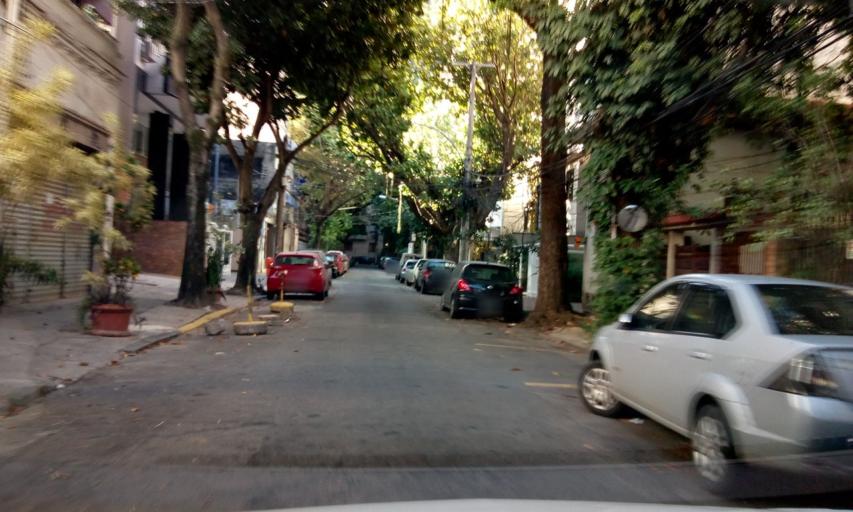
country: BR
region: Rio de Janeiro
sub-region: Rio De Janeiro
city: Rio de Janeiro
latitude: -22.9557
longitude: -43.1830
